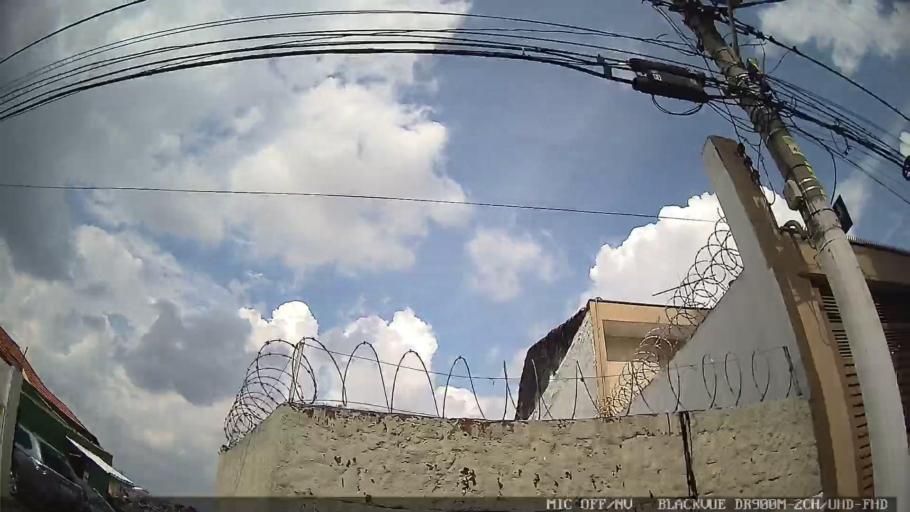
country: BR
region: Sao Paulo
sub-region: Braganca Paulista
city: Braganca Paulista
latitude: -22.9588
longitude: -46.5404
